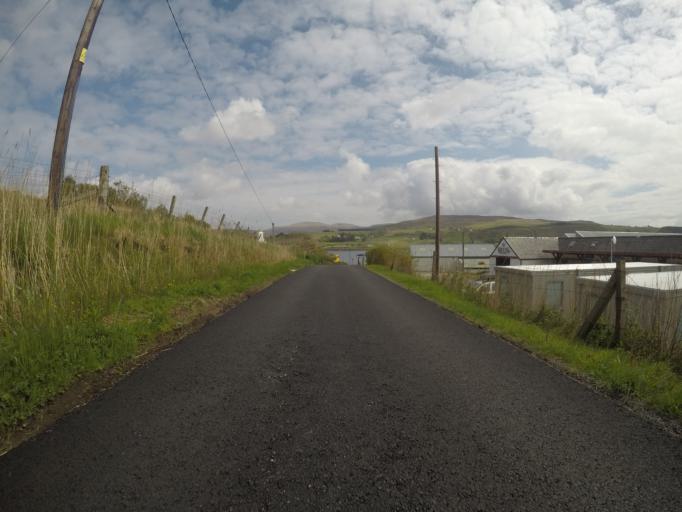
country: GB
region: Scotland
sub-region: Highland
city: Portree
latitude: 57.5878
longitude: -6.3775
